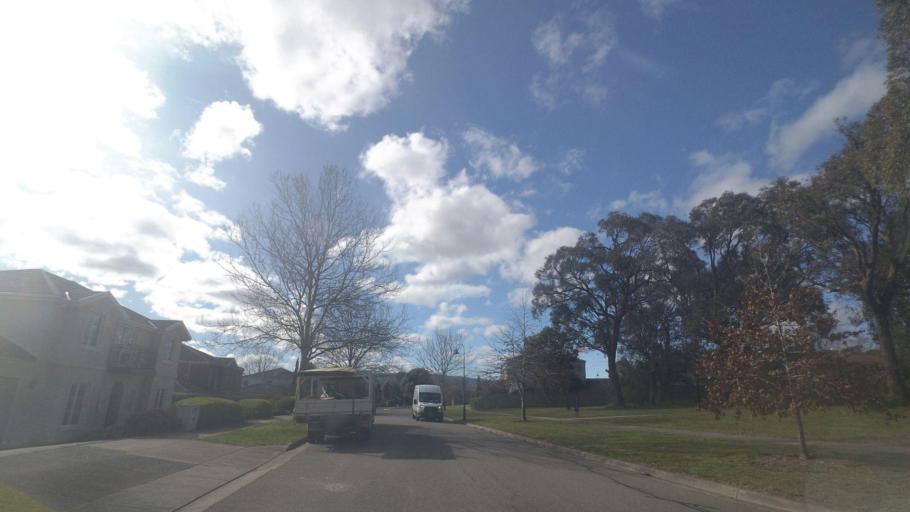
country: AU
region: Victoria
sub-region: Yarra Ranges
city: Lysterfield
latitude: -37.9254
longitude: 145.2712
